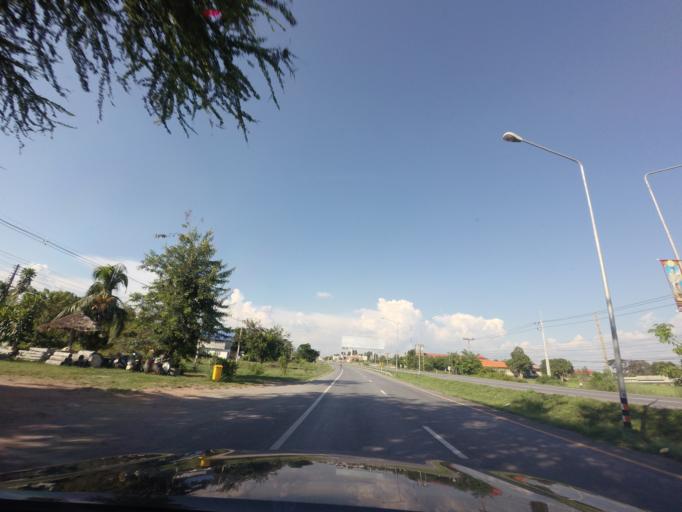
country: TH
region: Khon Kaen
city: Non Sila
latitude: 15.9602
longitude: 102.6890
